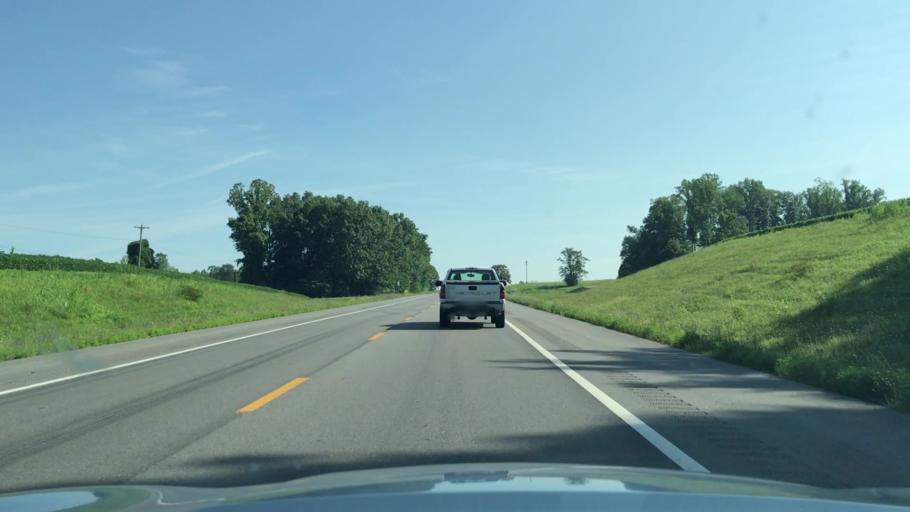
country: US
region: Tennessee
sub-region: Pickett County
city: Byrdstown
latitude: 36.4934
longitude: -85.1806
